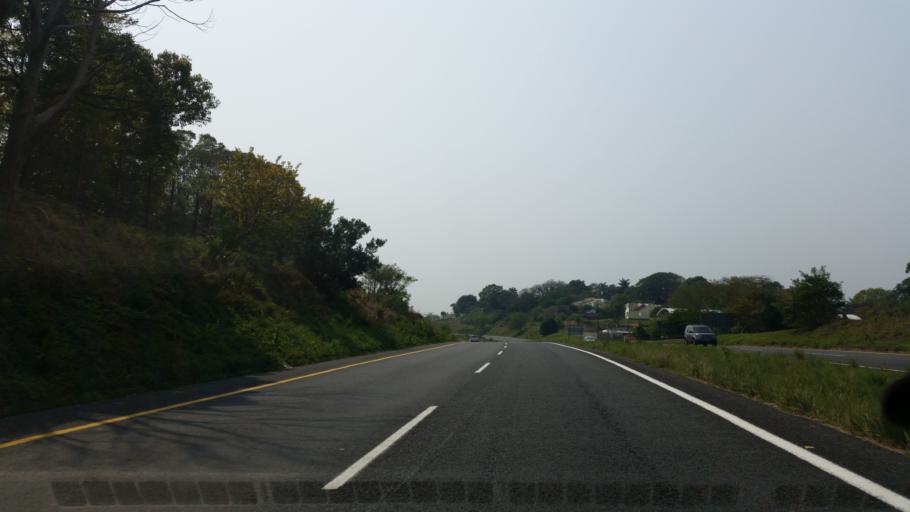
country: ZA
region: KwaZulu-Natal
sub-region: eThekwini Metropolitan Municipality
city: Berea
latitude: -29.8360
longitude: 30.9067
